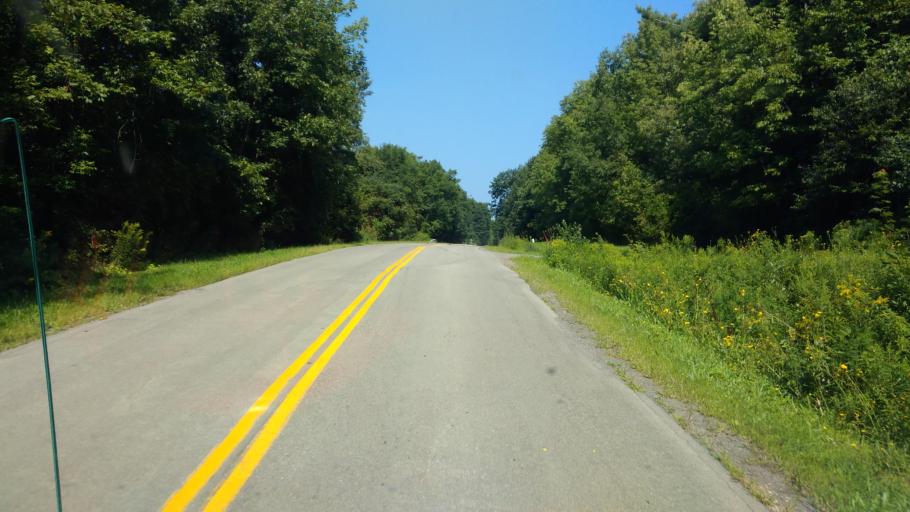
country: US
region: New York
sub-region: Allegany County
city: Belmont
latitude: 42.2733
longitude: -78.0533
